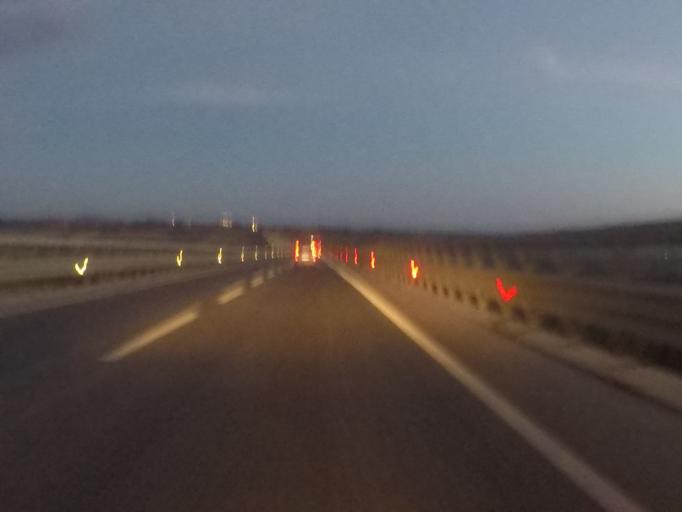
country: IT
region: Sicily
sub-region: Agrigento
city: Menfi
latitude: 37.5907
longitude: 13.0171
